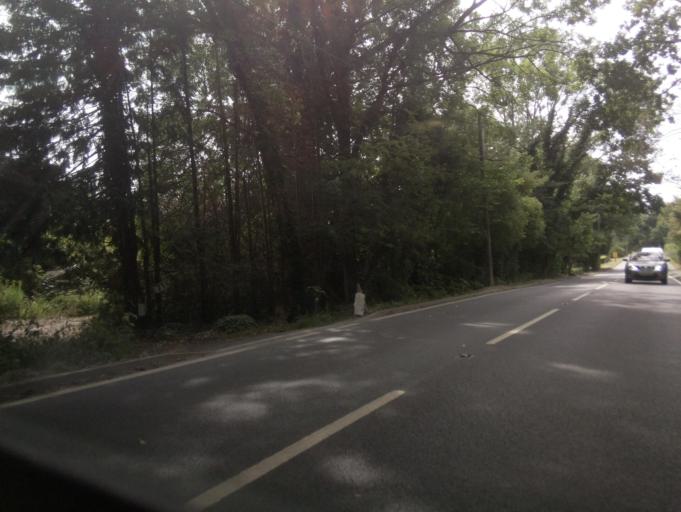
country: GB
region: England
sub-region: Surrey
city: Salfords
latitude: 51.1814
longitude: -0.1954
